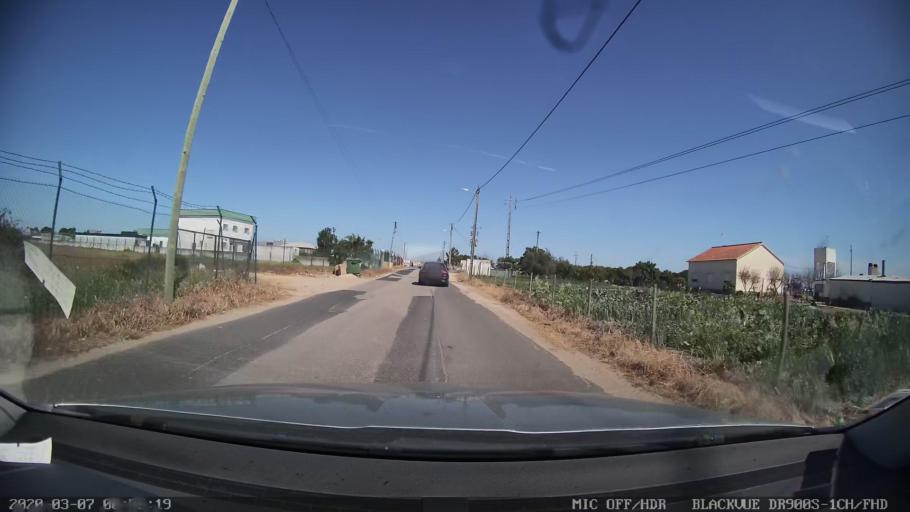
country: PT
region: Santarem
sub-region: Benavente
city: Benavente
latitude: 38.9589
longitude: -8.8170
